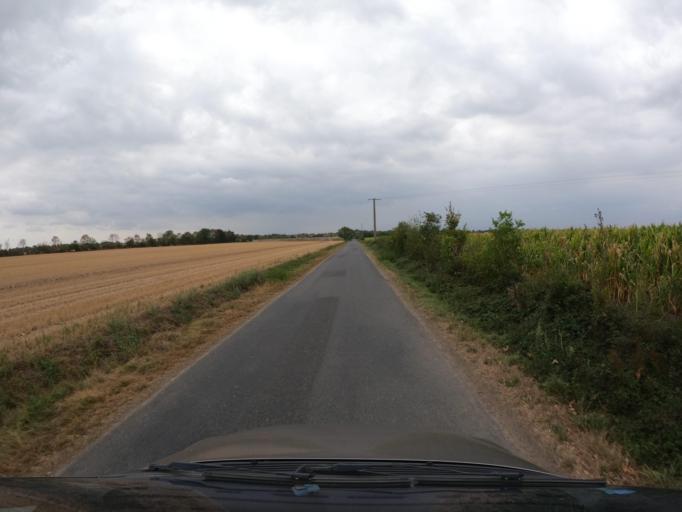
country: FR
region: Pays de la Loire
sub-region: Departement de la Vendee
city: La Bruffiere
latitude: 46.9901
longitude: -1.1590
